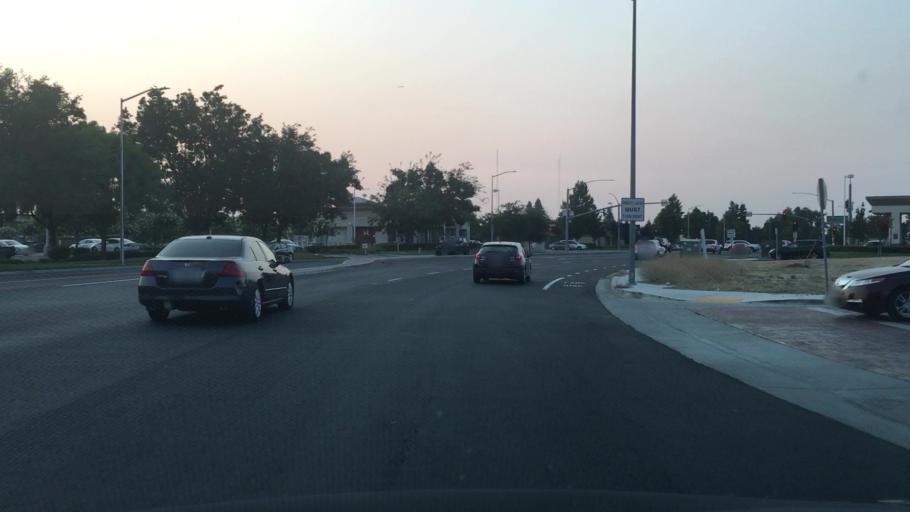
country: US
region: California
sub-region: Fresno County
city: Clovis
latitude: 36.8361
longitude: -119.6838
